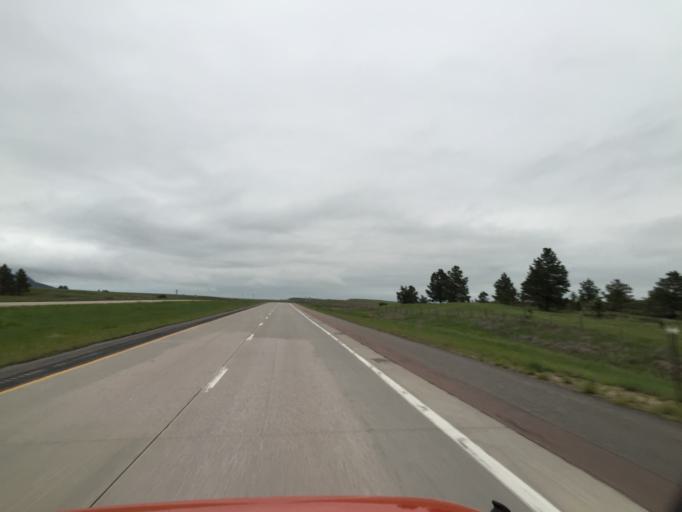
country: US
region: South Dakota
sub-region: Fall River County
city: Hot Springs
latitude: 43.4466
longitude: -103.3590
